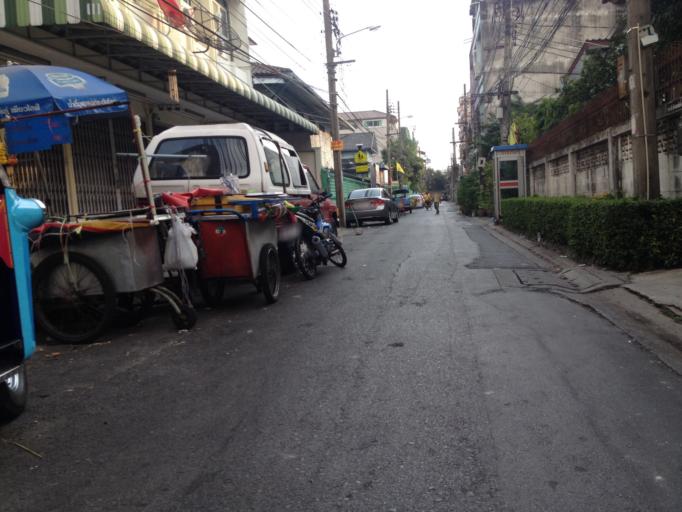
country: TH
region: Bangkok
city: Phra Nakhon
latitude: 13.7679
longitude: 100.5044
